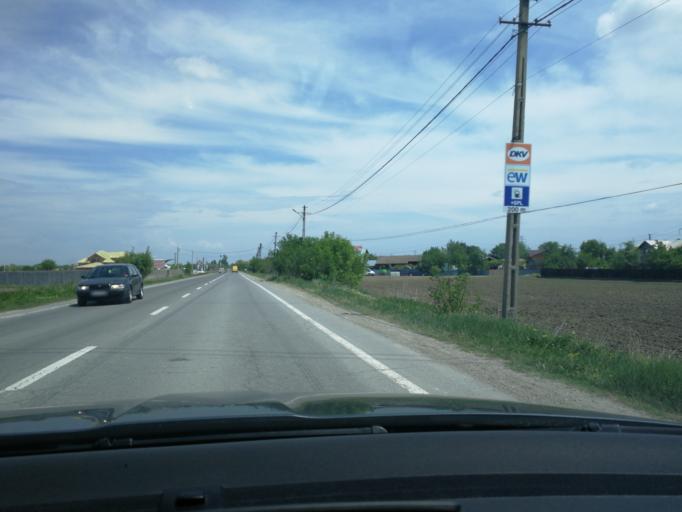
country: RO
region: Prahova
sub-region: Comuna Targsoru Vechi
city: Targsoru Vechi
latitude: 44.8602
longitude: 25.9263
